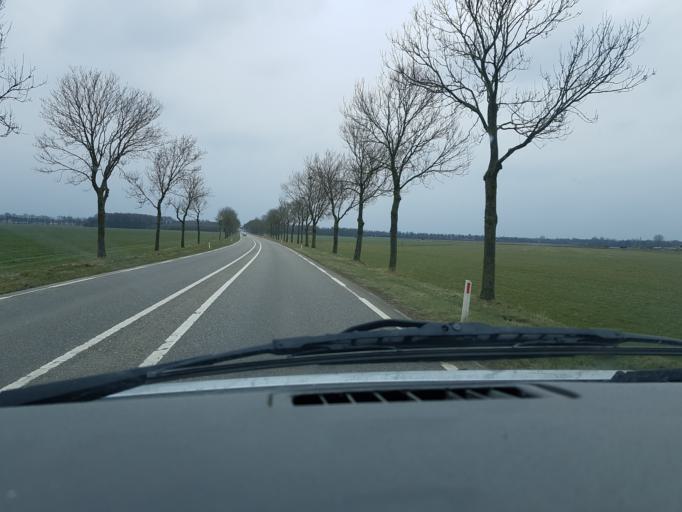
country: NL
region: Gelderland
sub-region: Gemeente Wijchen
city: Wijchen
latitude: 51.8369
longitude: 5.7362
